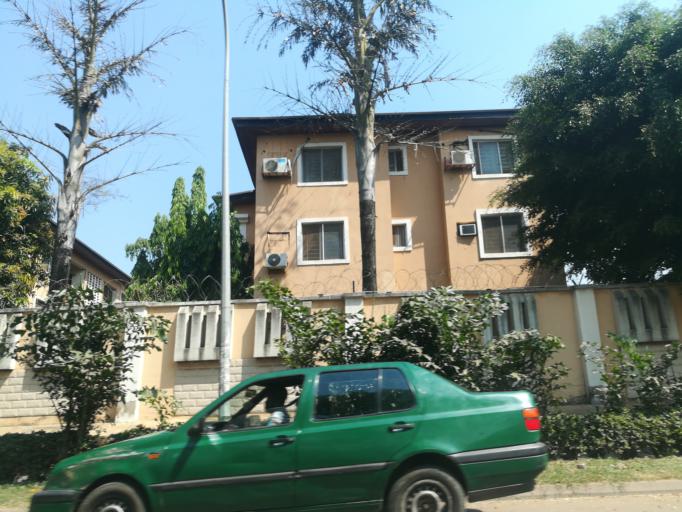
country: NG
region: Abuja Federal Capital Territory
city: Abuja
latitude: 9.0708
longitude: 7.4437
